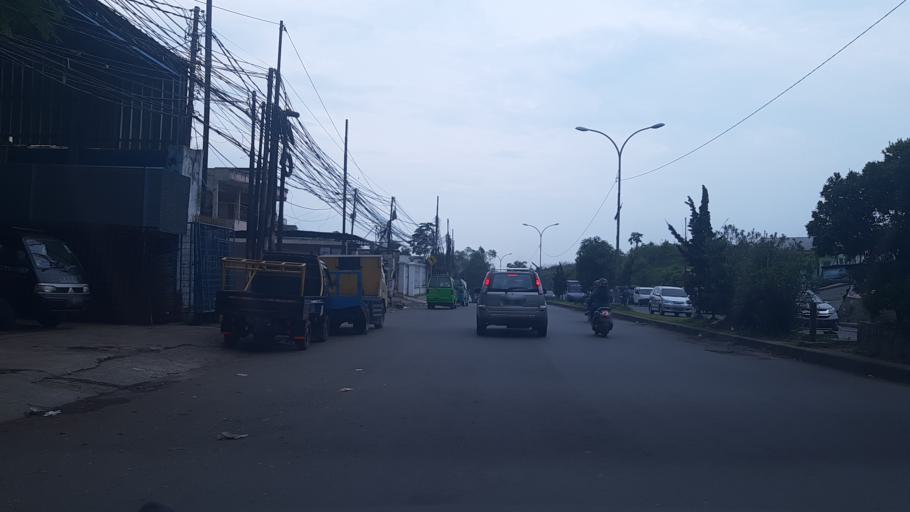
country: ID
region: West Java
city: Citeureup
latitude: -6.4832
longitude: 106.8701
